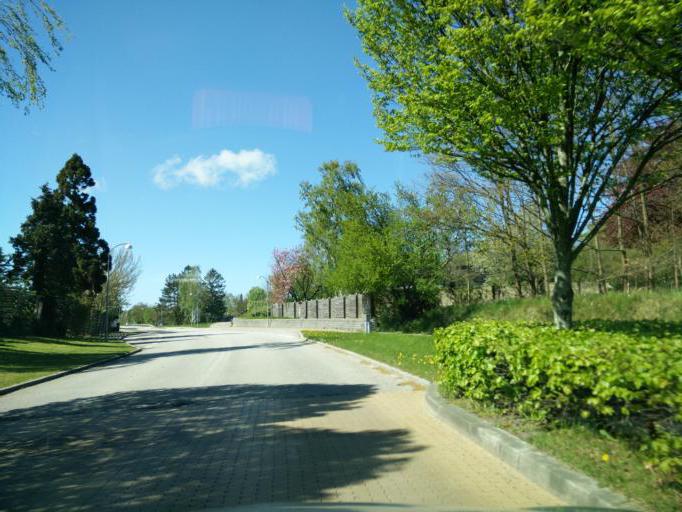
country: DK
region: Capital Region
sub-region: Gribskov Kommune
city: Helsinge
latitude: 56.0097
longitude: 12.2177
